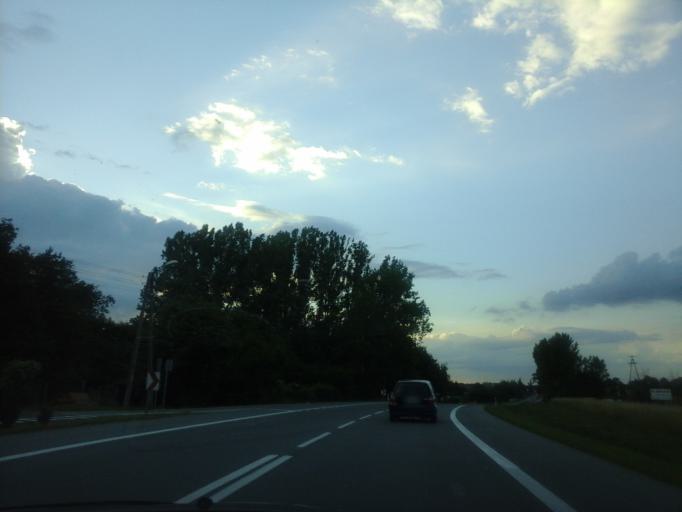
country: PL
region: Lubusz
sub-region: Powiat nowosolski
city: Nowe Miasteczko
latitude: 51.6972
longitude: 15.7295
